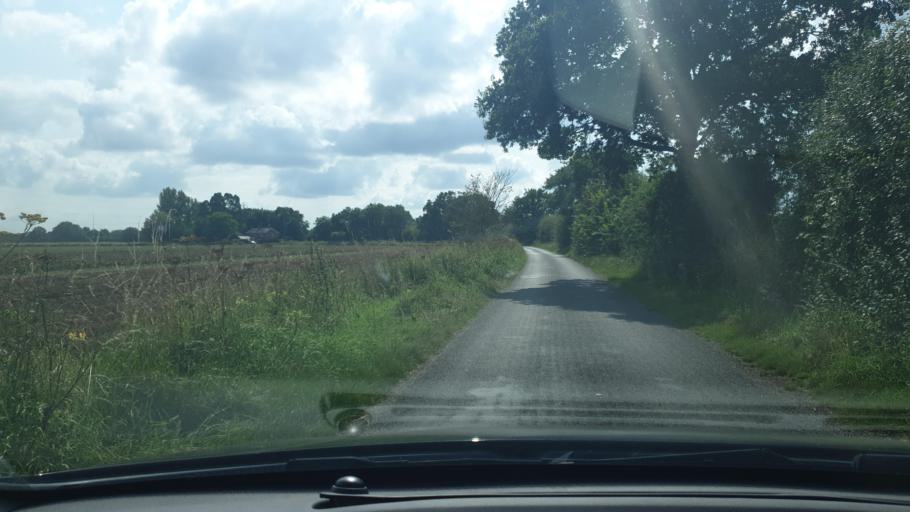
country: GB
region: England
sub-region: Essex
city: Manningtree
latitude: 51.9170
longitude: 1.0107
